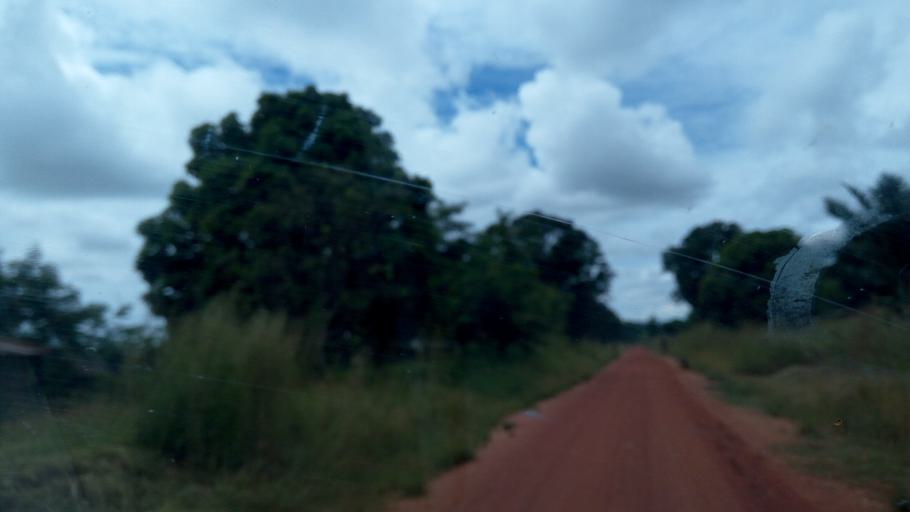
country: CD
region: Katanga
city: Kalemie
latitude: -5.9931
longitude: 29.0716
